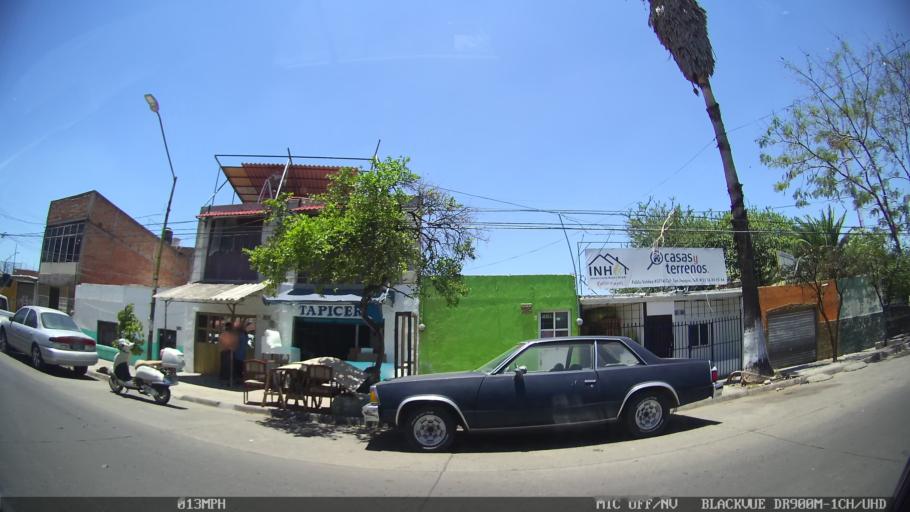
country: MX
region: Jalisco
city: Tlaquepaque
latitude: 20.6738
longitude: -103.2792
